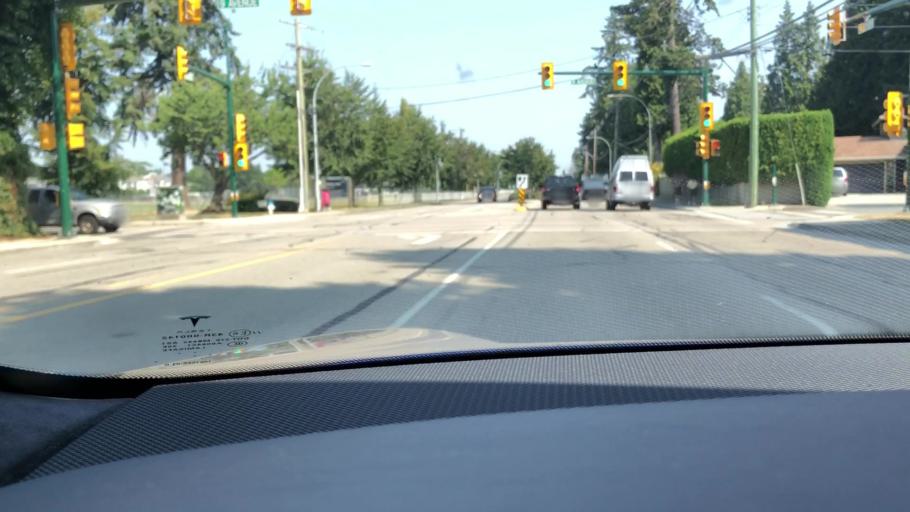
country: US
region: Washington
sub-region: Whatcom County
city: Point Roberts
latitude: 49.0189
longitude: -123.0686
